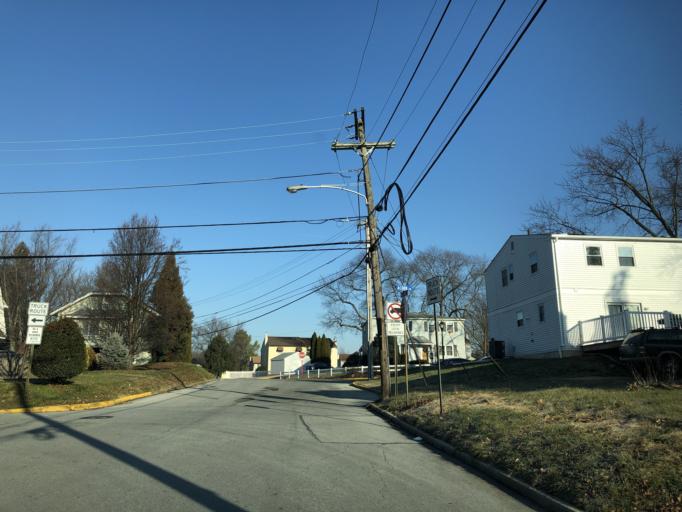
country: US
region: Pennsylvania
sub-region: Chester County
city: Downingtown
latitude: 40.0062
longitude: -75.6914
